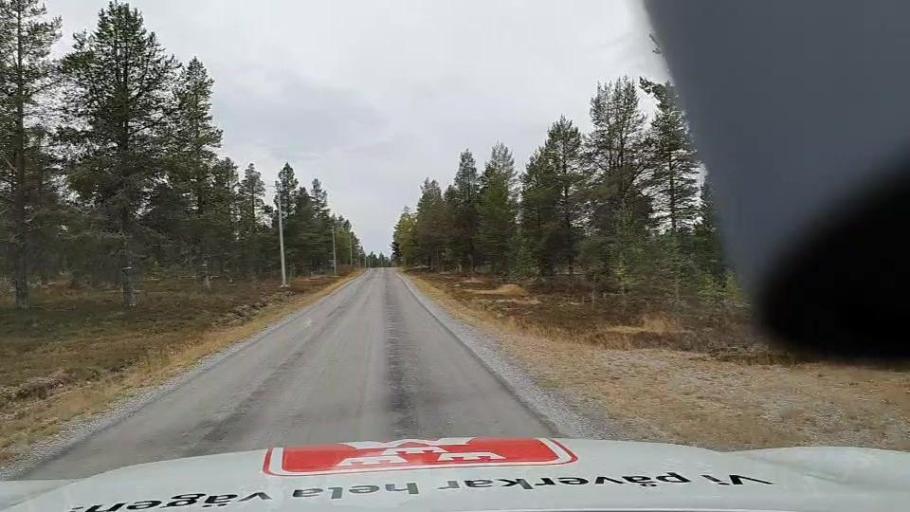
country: NO
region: Hedmark
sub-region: Engerdal
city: Engerdal
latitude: 62.0952
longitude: 12.8279
